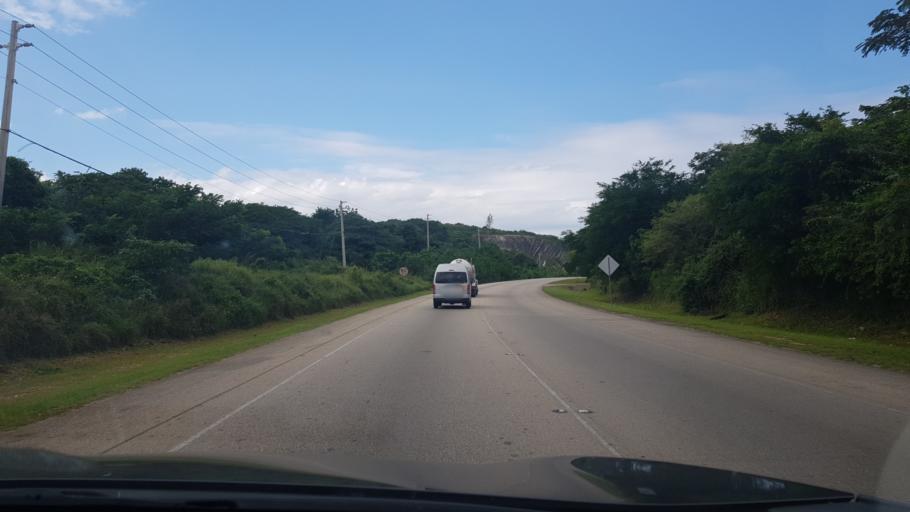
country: JM
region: Trelawny
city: Duncans
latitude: 18.4750
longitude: -77.5892
